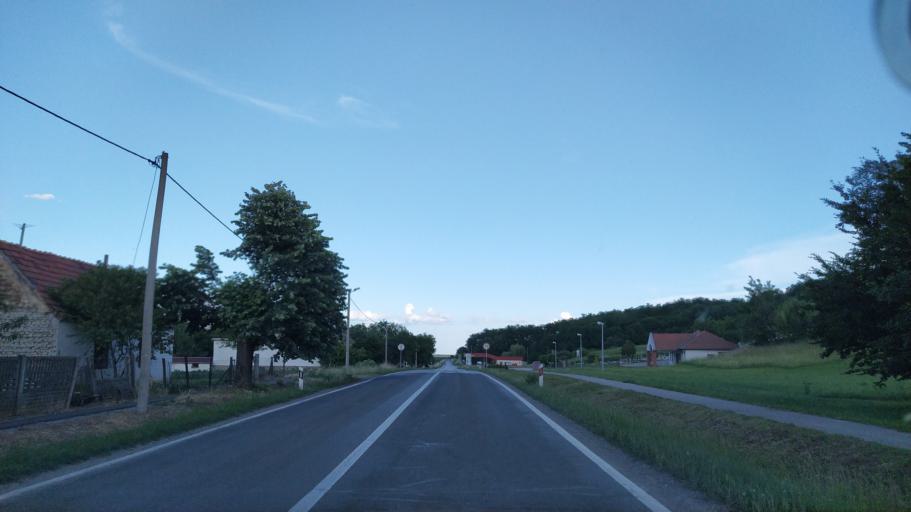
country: HR
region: Virovitick-Podravska
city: Suhopolje
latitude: 45.7497
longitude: 17.5866
